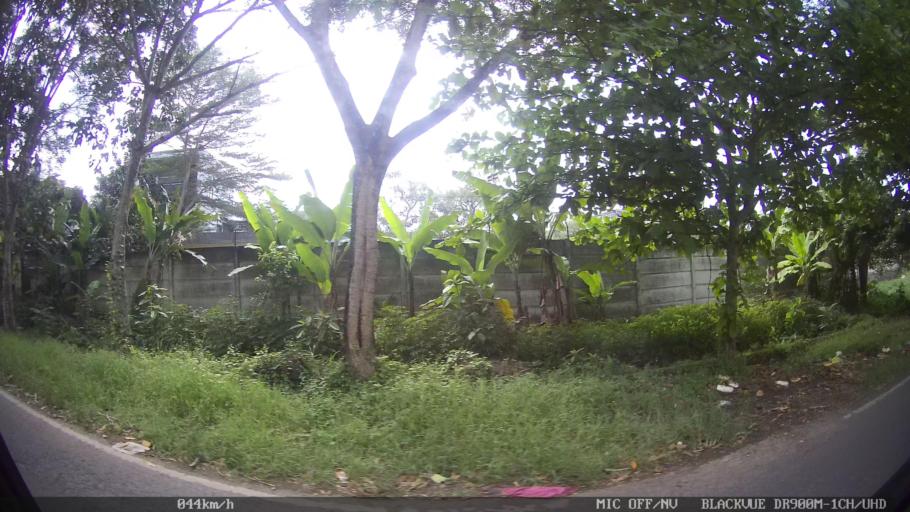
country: ID
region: Lampung
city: Bandarlampung
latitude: -5.4468
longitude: 105.2426
